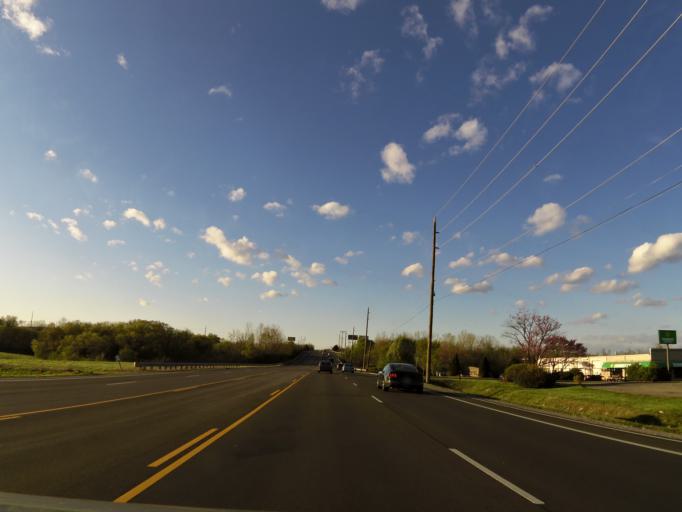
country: US
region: Tennessee
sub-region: Davidson County
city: Goodlettsville
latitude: 36.2844
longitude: -86.6925
